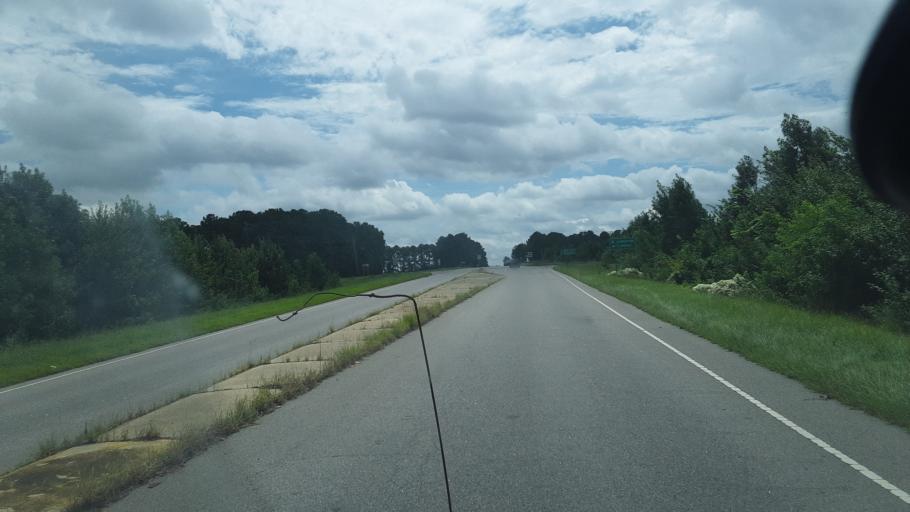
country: US
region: North Carolina
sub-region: Robeson County
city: Rowland
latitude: 34.5261
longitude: -79.2780
